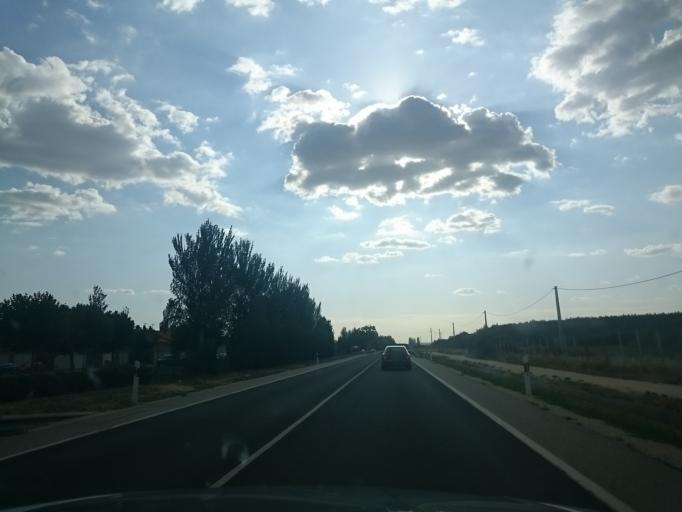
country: ES
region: Castille and Leon
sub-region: Provincia de Burgos
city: Los Tomillares
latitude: 42.3332
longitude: -3.5618
